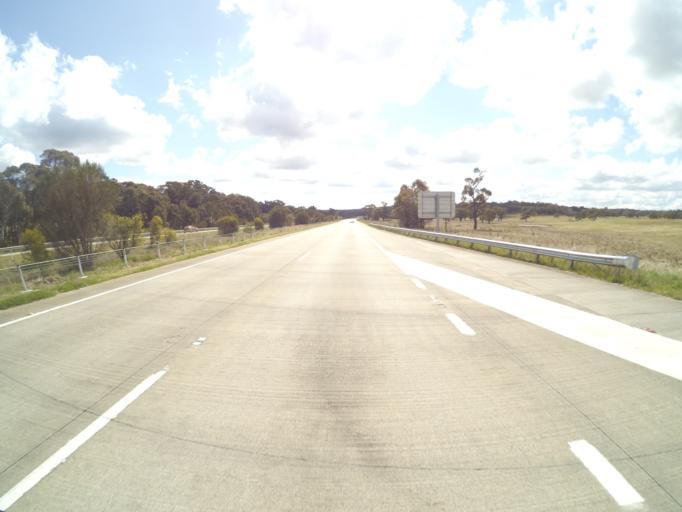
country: AU
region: New South Wales
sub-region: Wingecarribee
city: Moss Vale
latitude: -34.4904
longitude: 150.3119
